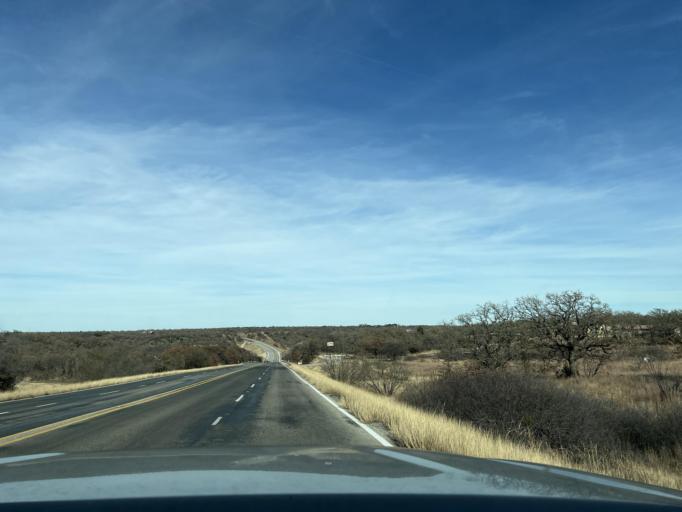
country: US
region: Texas
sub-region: Eastland County
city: Cisco
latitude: 32.4317
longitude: -98.9839
